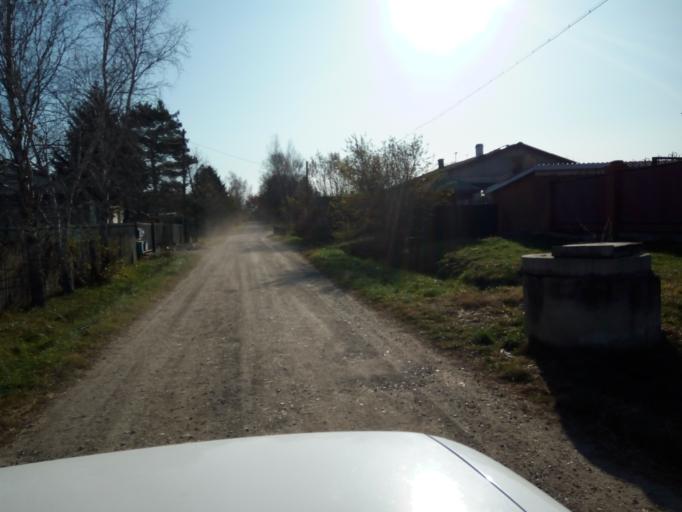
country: RU
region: Primorskiy
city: Lazo
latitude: 45.8668
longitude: 133.6484
